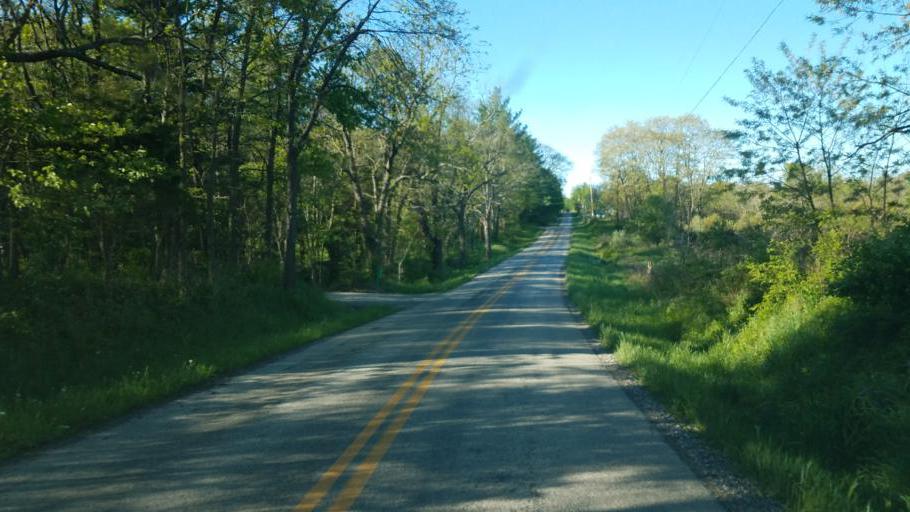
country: US
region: Ohio
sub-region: Delaware County
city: Sunbury
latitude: 40.3530
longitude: -82.8187
